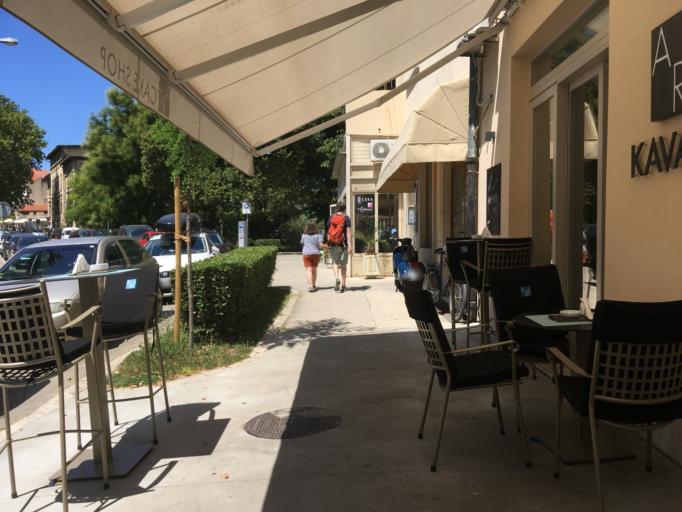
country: HR
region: Zadarska
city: Zadar
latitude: 44.1126
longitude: 15.2310
